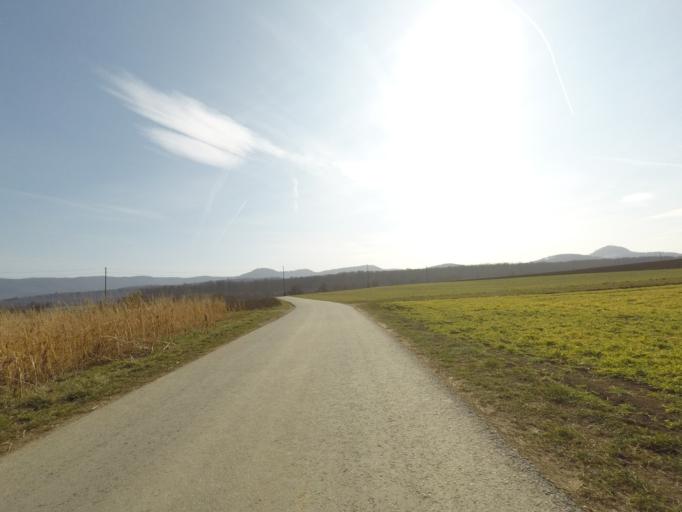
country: DE
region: Baden-Wuerttemberg
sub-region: Tuebingen Region
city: Metzingen
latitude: 48.5324
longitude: 9.2601
